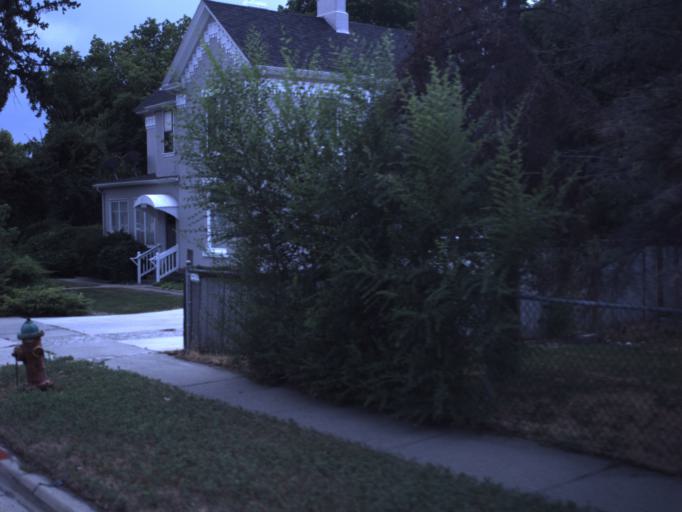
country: US
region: Utah
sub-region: Salt Lake County
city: Millcreek
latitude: 40.7042
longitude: -111.8715
